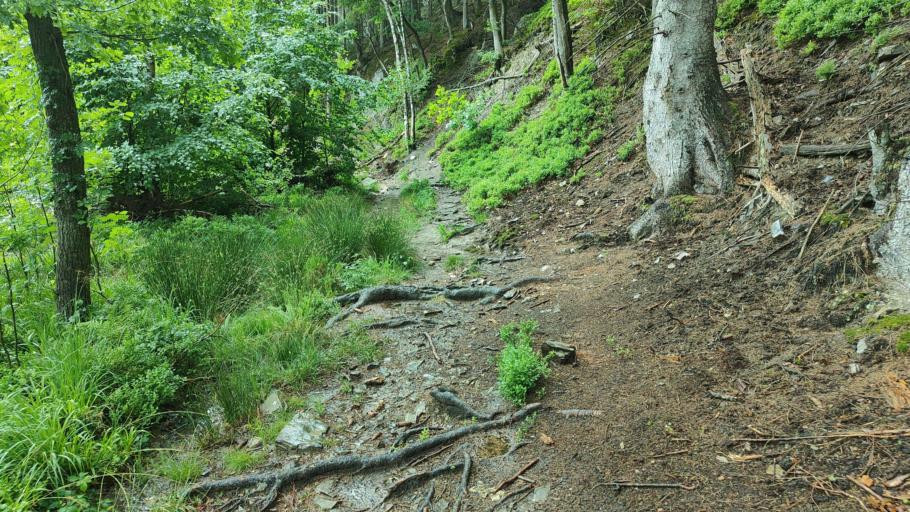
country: DE
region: North Rhine-Westphalia
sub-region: Regierungsbezirk Koln
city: Roetgen
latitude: 50.6236
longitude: 6.1635
